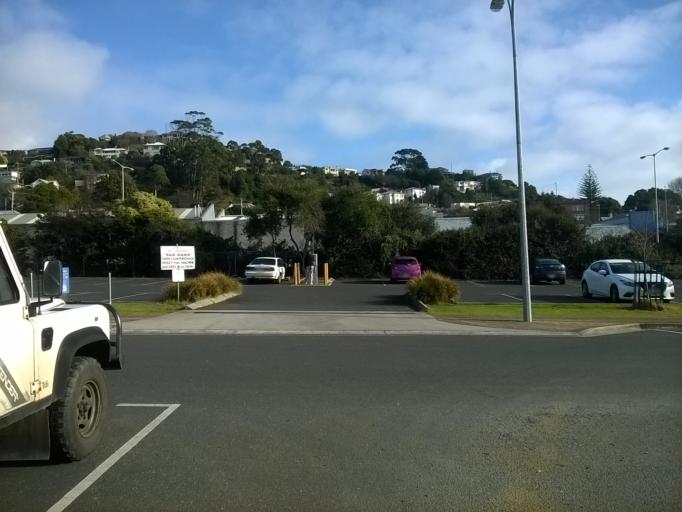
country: AU
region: Tasmania
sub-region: Burnie
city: Burnie
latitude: -41.0497
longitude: 145.9027
